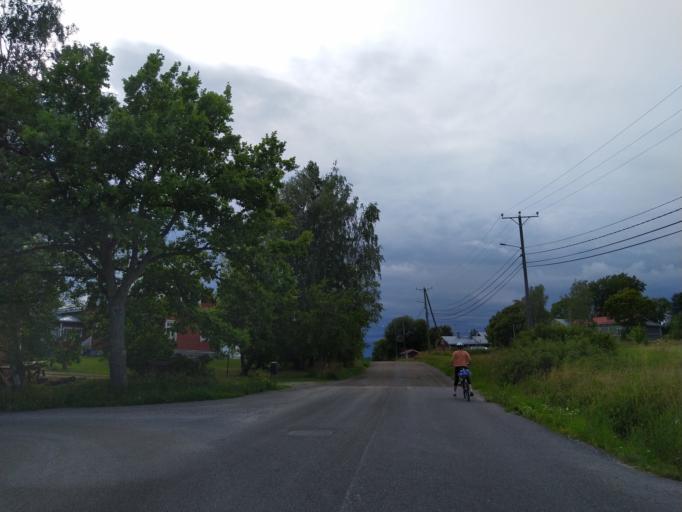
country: FI
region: Varsinais-Suomi
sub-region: Turku
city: Raisio
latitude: 60.4272
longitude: 22.2029
